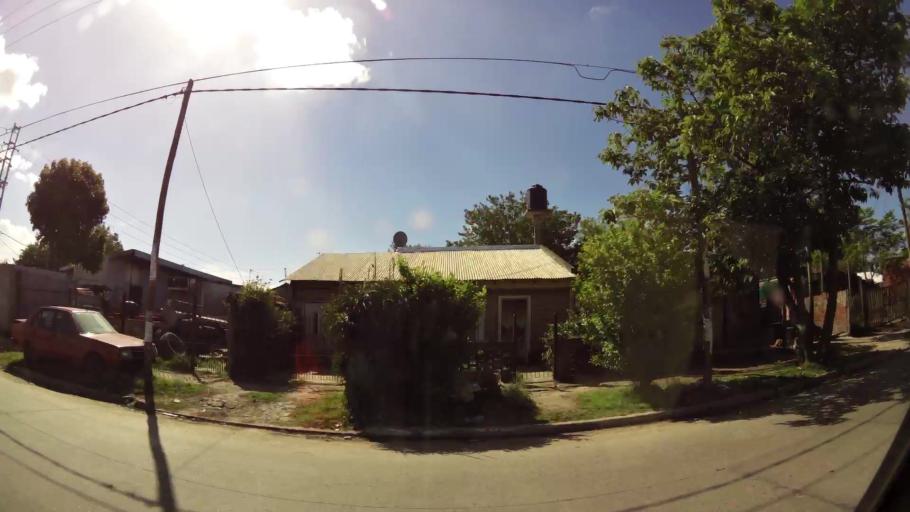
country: AR
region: Buenos Aires
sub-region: Partido de Quilmes
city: Quilmes
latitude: -34.7995
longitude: -58.2629
